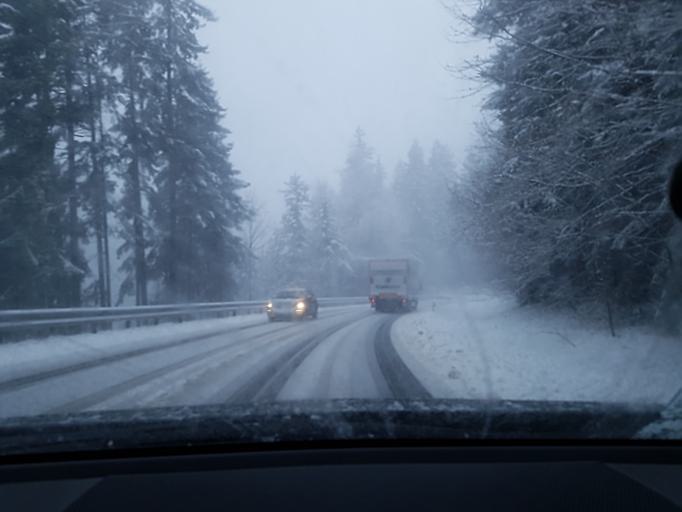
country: AT
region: Salzburg
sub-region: Politischer Bezirk Hallein
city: Abtenau
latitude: 47.5812
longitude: 13.3207
